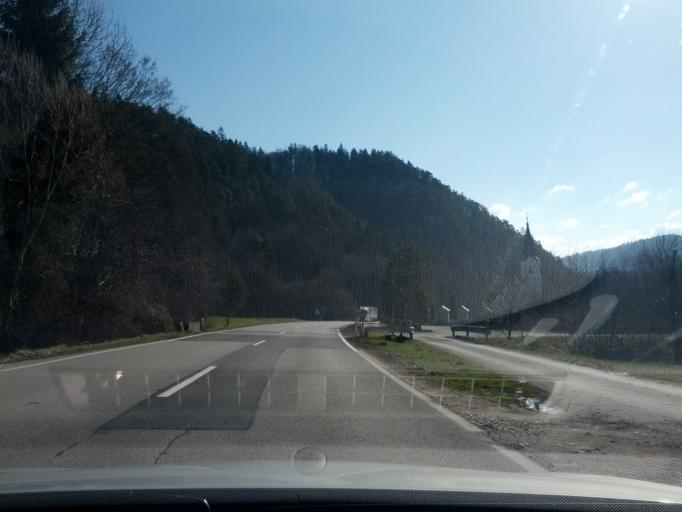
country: SI
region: Moravce
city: Moravce
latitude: 46.0960
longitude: 14.6892
